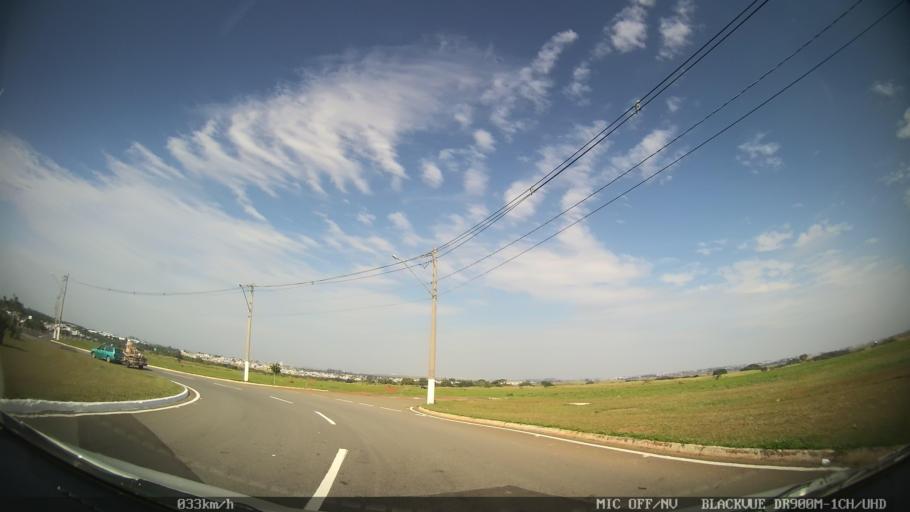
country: BR
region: Sao Paulo
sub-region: Paulinia
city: Paulinia
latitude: -22.7847
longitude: -47.1525
